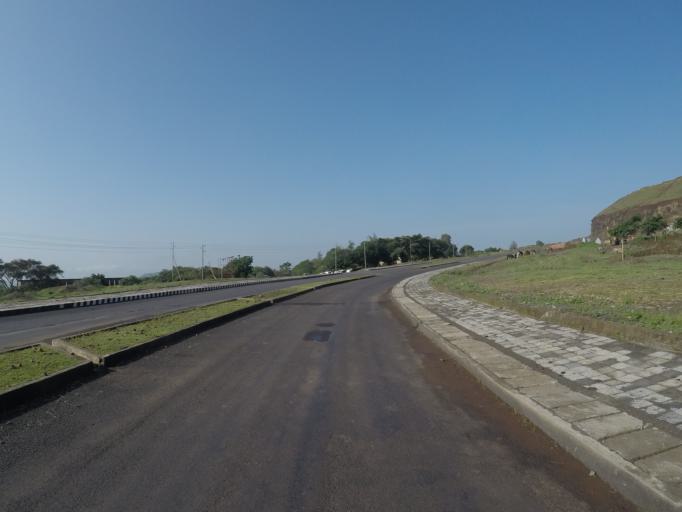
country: ET
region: Amhara
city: Gondar
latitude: 12.5232
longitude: 37.4311
